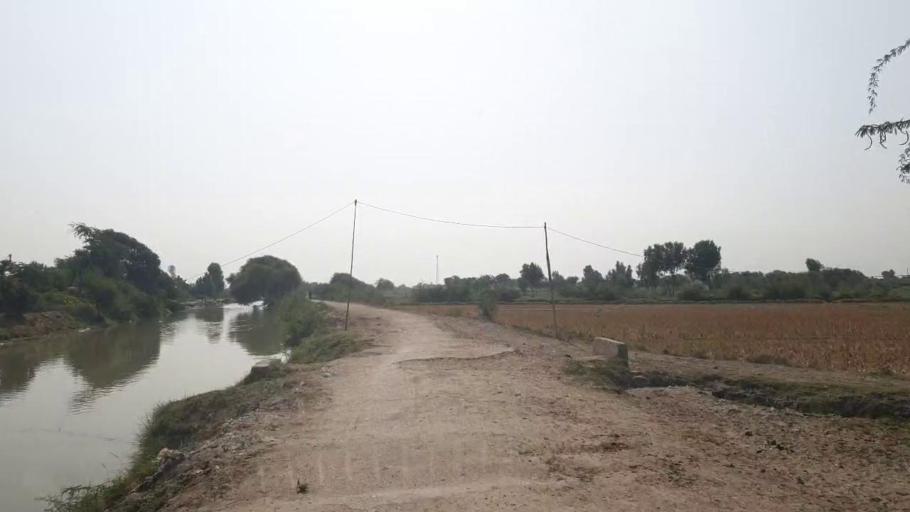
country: PK
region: Sindh
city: Badin
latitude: 24.6468
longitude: 68.8466
